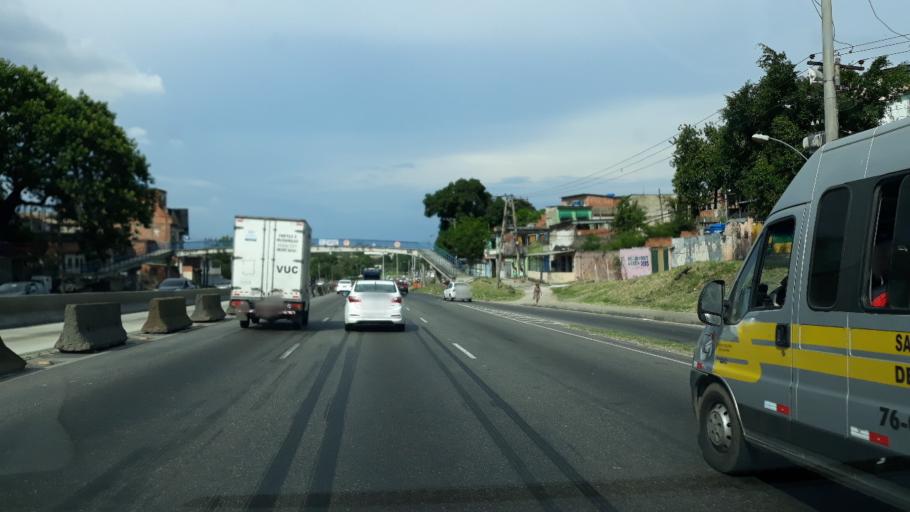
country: BR
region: Rio de Janeiro
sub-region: Sao Joao De Meriti
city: Sao Joao de Meriti
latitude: -22.8360
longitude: -43.3624
